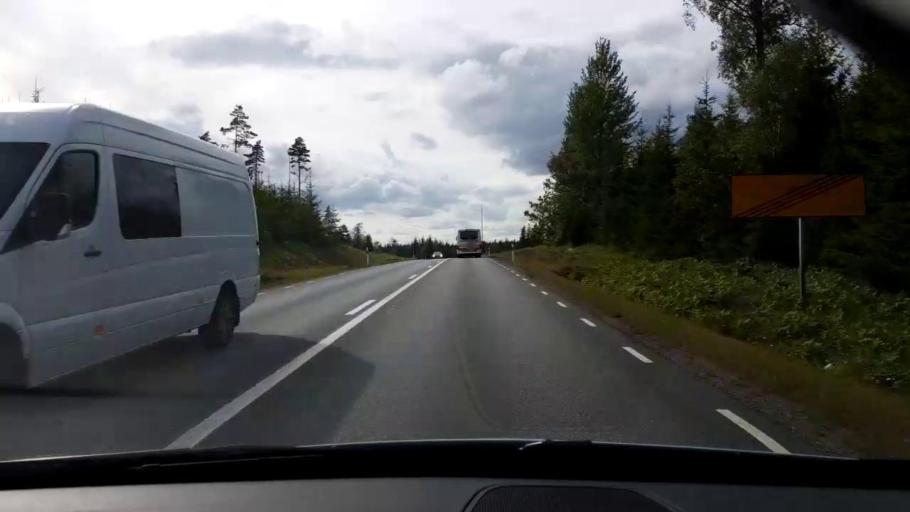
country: SE
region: Joenkoeping
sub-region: Savsjo Kommun
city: Saevsjoe
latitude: 57.3931
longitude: 14.7223
